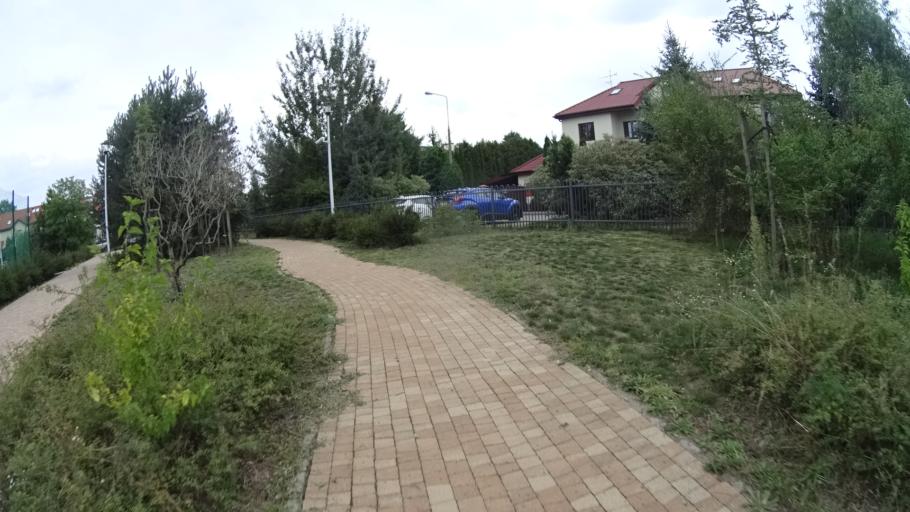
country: PL
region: Masovian Voivodeship
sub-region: Powiat pruszkowski
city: Nadarzyn
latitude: 52.1053
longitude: 20.8002
